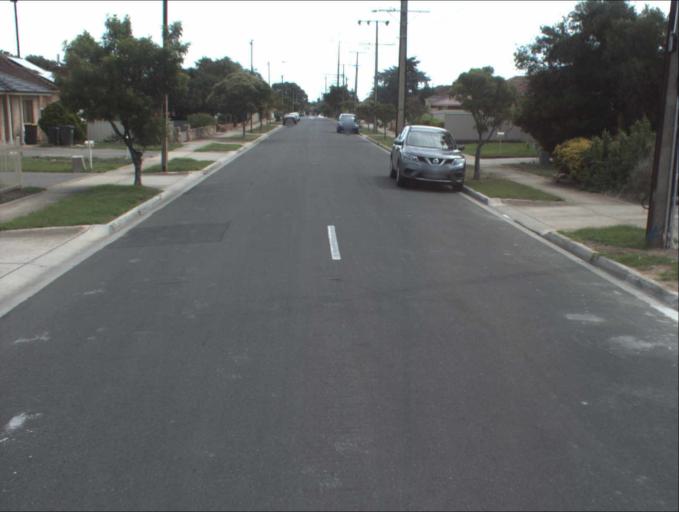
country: AU
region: South Australia
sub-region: Port Adelaide Enfield
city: Enfield
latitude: -34.8604
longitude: 138.6168
